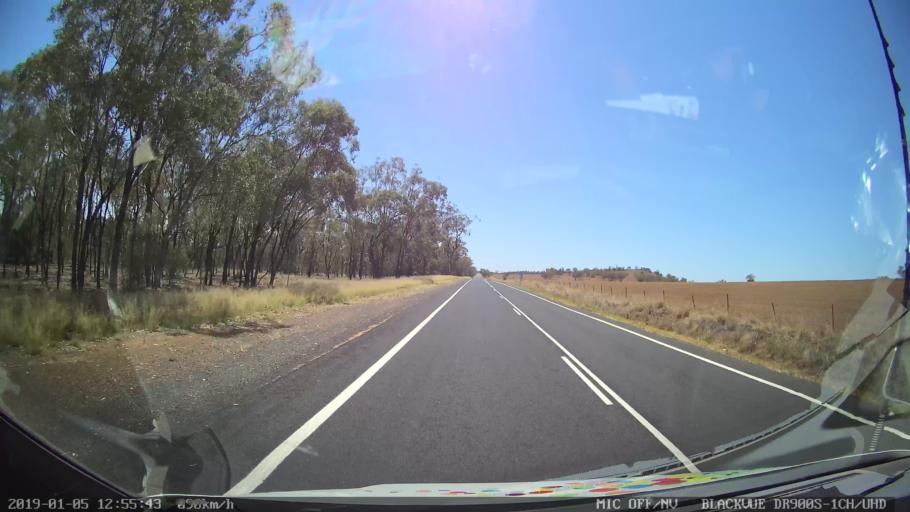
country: AU
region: New South Wales
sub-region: Warrumbungle Shire
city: Coonabarabran
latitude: -31.1197
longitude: 149.7103
